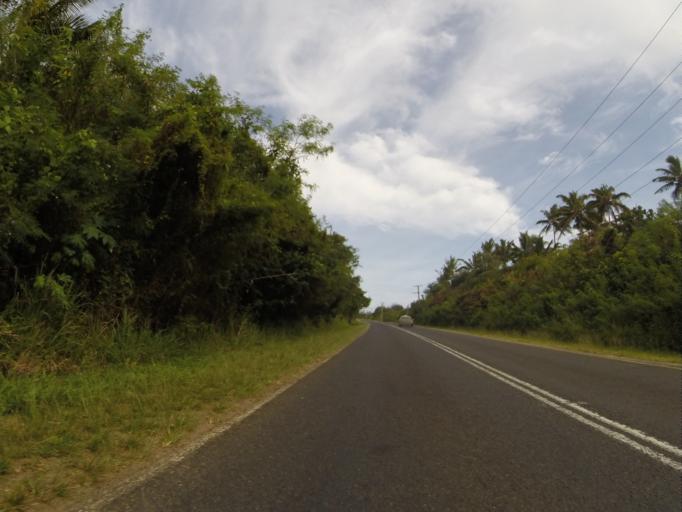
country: FJ
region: Western
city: Nadi
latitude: -18.1646
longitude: 177.4662
